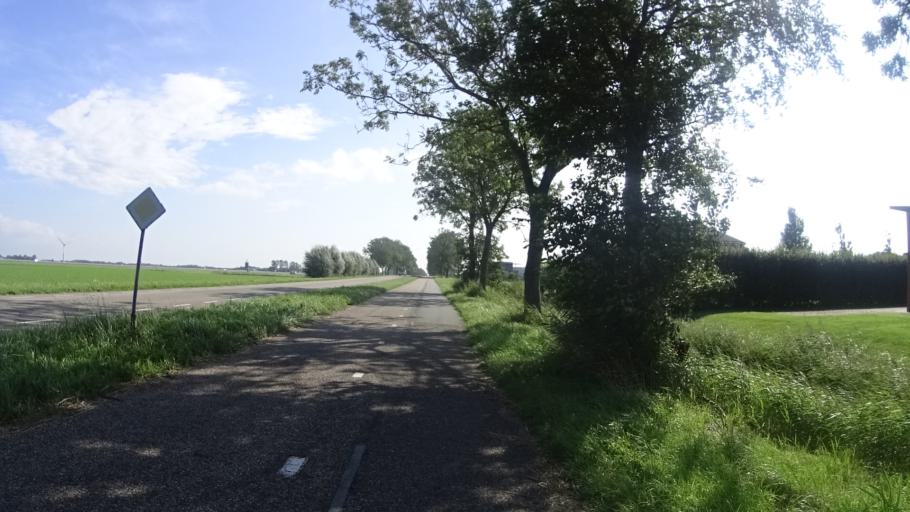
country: NL
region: Friesland
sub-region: Menameradiel
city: Dronryp
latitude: 53.1972
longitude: 5.6279
